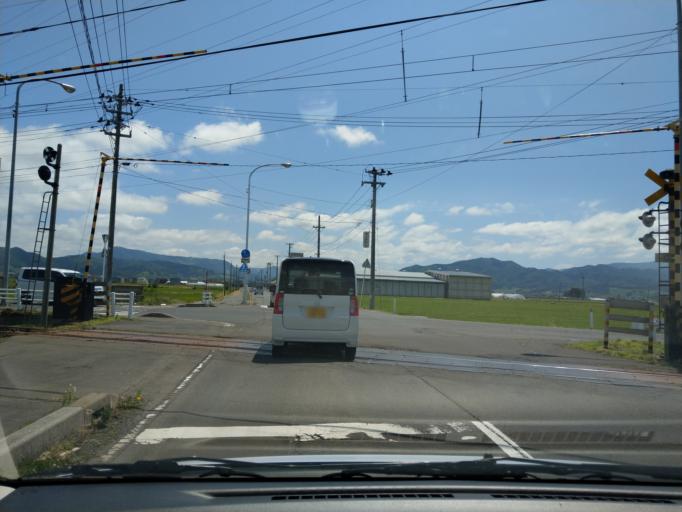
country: JP
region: Aomori
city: Kuroishi
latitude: 40.5820
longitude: 140.5509
